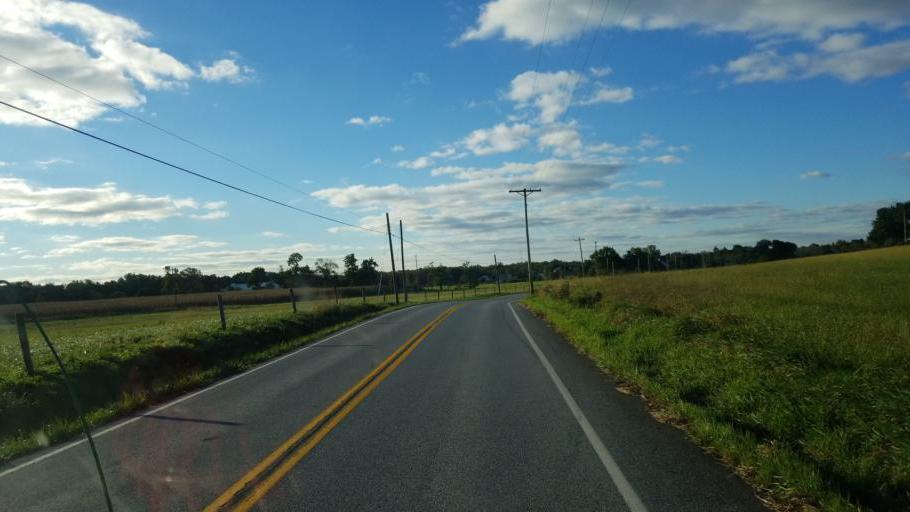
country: US
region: Pennsylvania
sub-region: Adams County
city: Gettysburg
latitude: 39.8628
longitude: -77.2281
